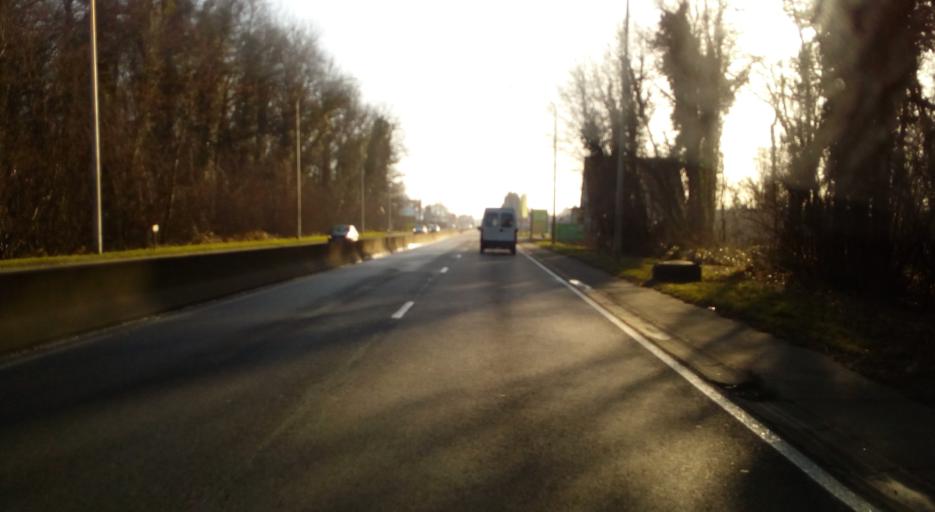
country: BE
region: Wallonia
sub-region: Province du Hainaut
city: Gerpinnes
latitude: 50.3481
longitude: 4.4724
